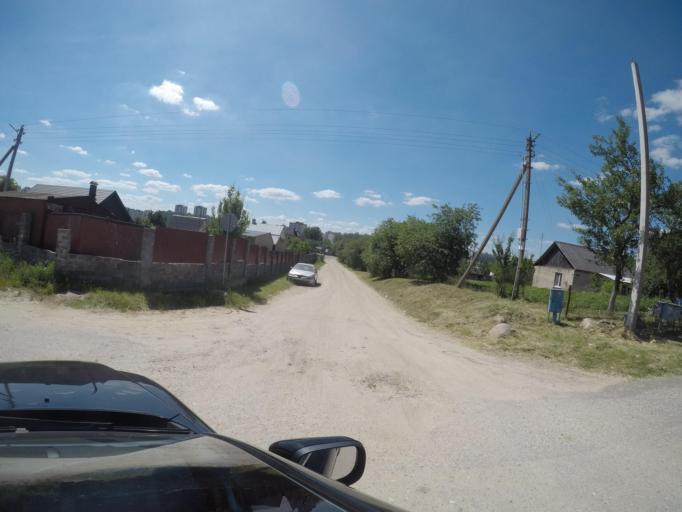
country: BY
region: Grodnenskaya
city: Hrodna
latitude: 53.7204
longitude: 23.8512
